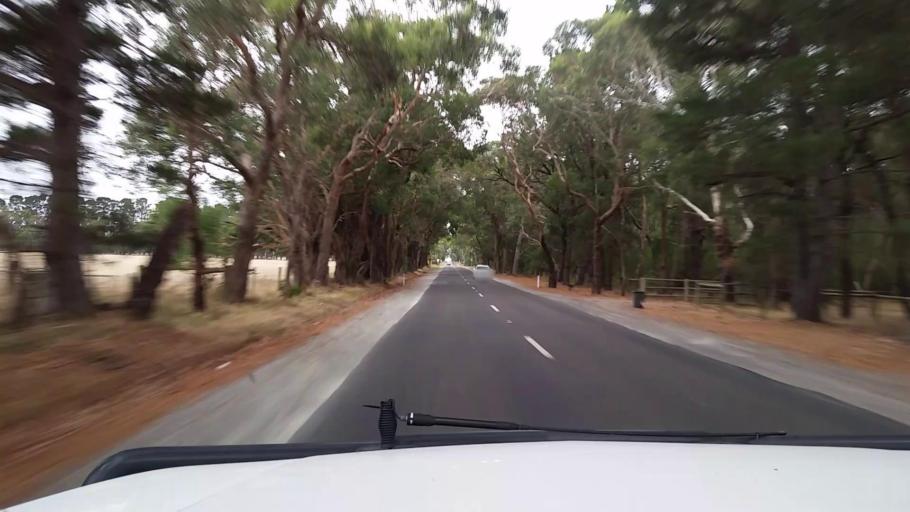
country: AU
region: Victoria
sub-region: Mornington Peninsula
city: Balnarring
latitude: -38.3268
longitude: 145.1457
